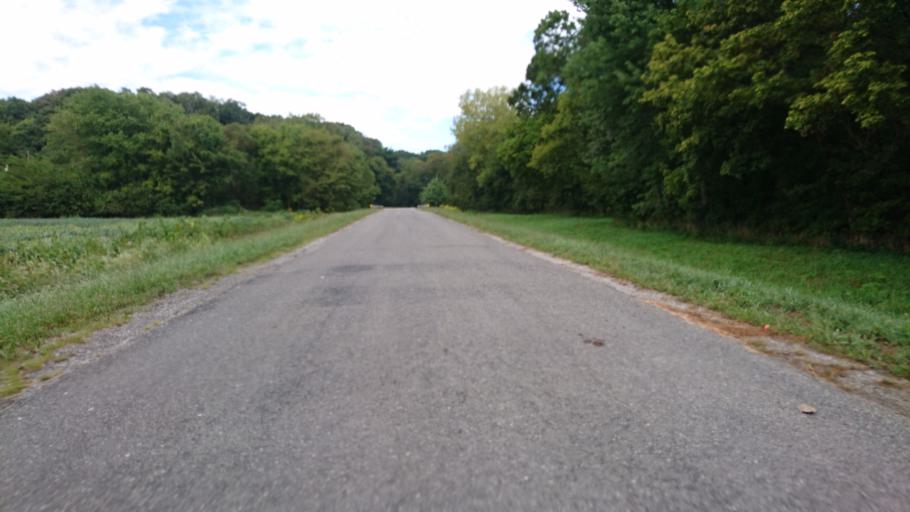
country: US
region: Illinois
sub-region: Macoupin County
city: Staunton
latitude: 38.9896
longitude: -89.7107
